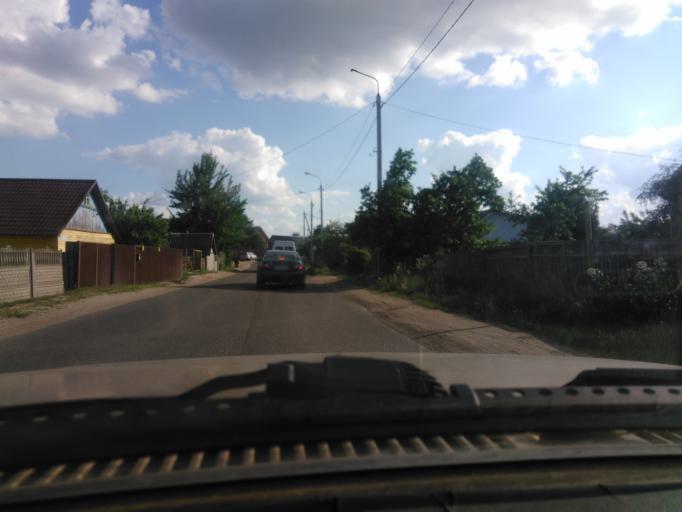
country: BY
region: Mogilev
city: Mahilyow
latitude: 53.9314
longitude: 30.3218
